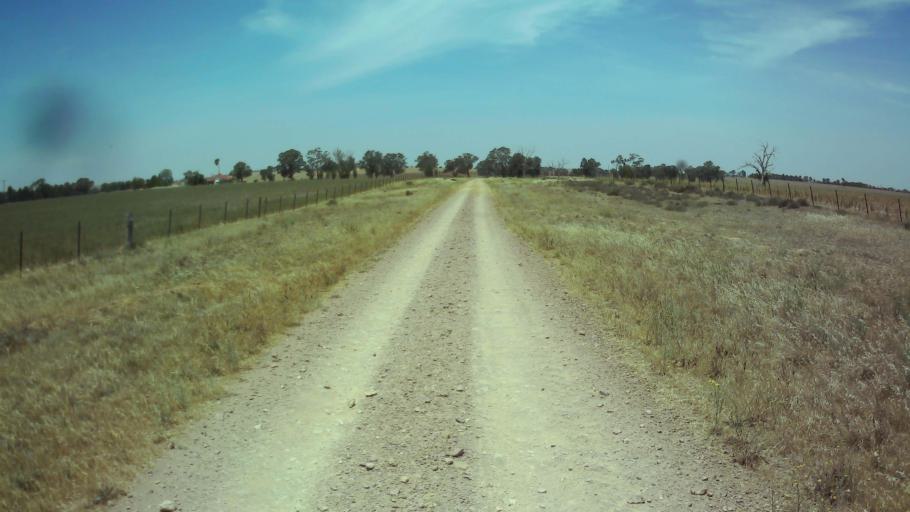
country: AU
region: New South Wales
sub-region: Weddin
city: Grenfell
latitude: -34.0016
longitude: 148.3978
